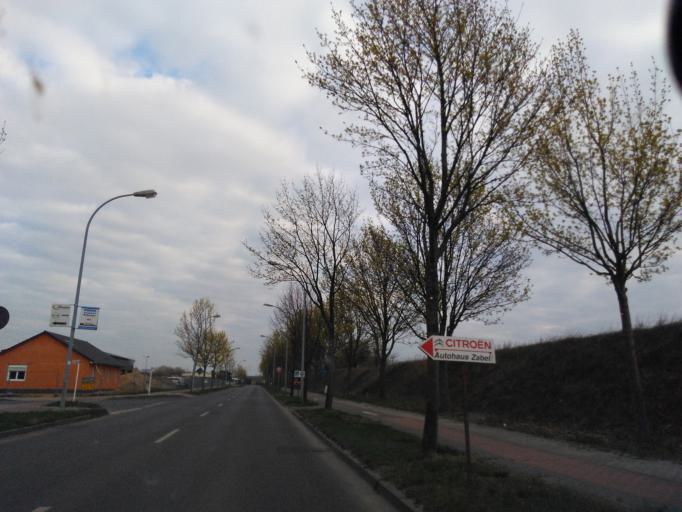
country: DE
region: Brandenburg
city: Strausberg
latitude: 52.5806
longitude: 13.9083
